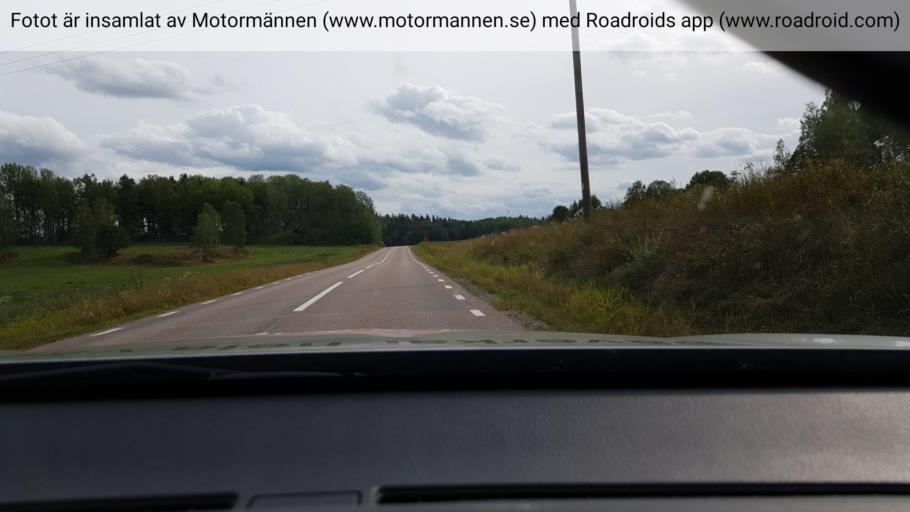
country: SE
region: Soedermanland
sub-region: Gnesta Kommun
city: Gnesta
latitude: 59.0423
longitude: 17.1618
